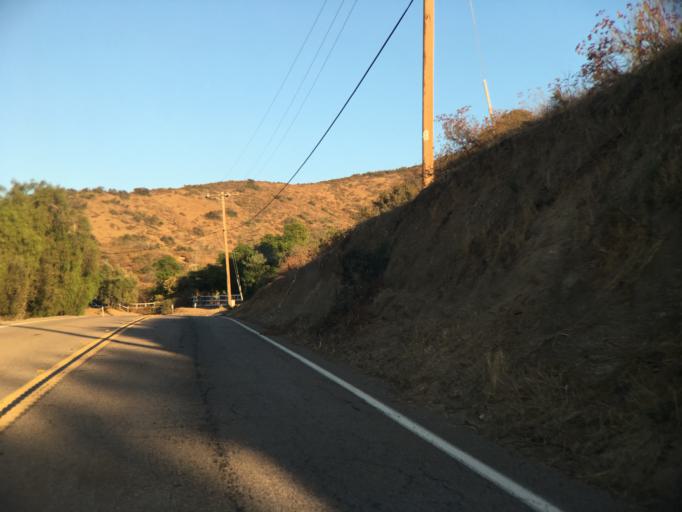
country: US
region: California
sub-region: San Diego County
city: Harbison Canyon
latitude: 32.8046
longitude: -116.8120
